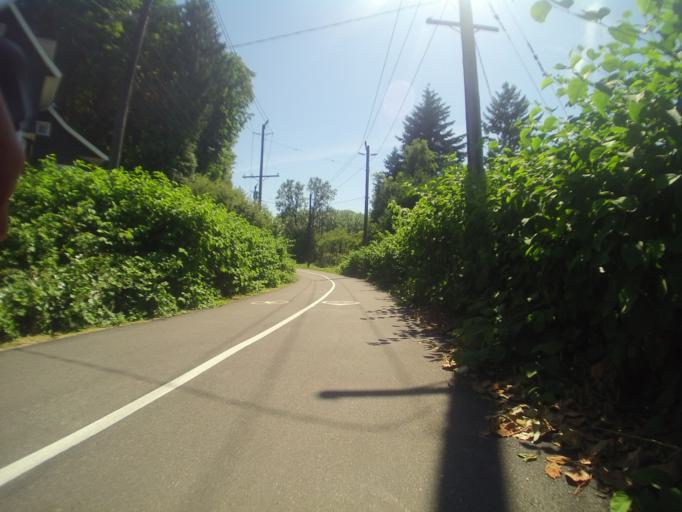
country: CA
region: British Columbia
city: Vancouver
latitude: 49.2406
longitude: -123.1541
